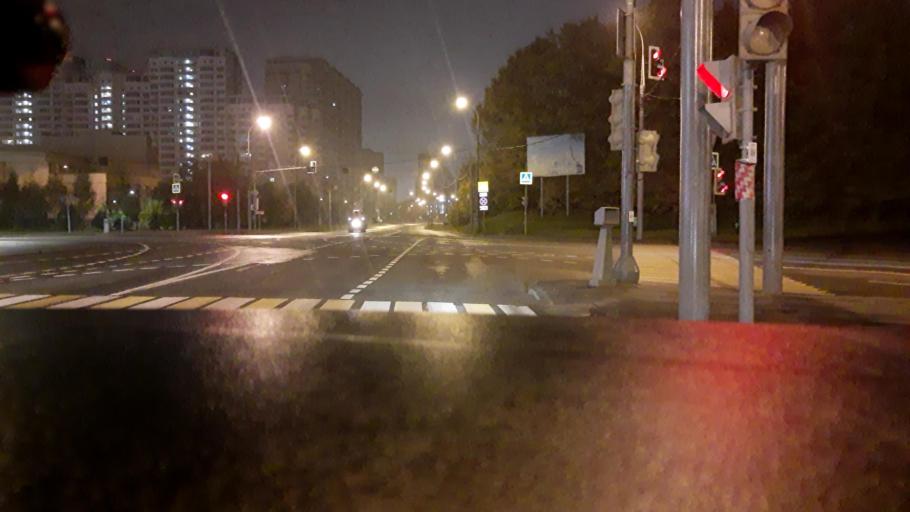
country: RU
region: Moskovskaya
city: Pavshino
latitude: 55.8419
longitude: 37.3719
